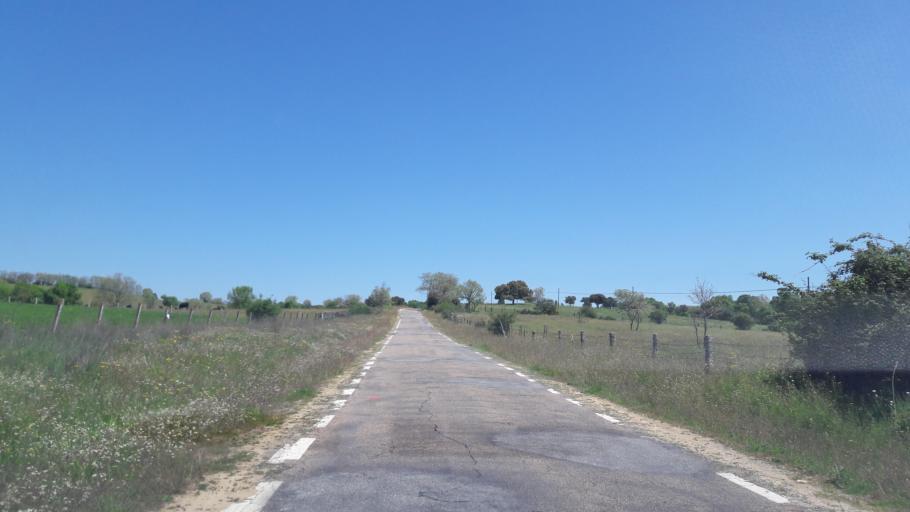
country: ES
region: Castille and Leon
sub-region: Provincia de Salamanca
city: Endrinal
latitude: 40.5687
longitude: -5.8076
